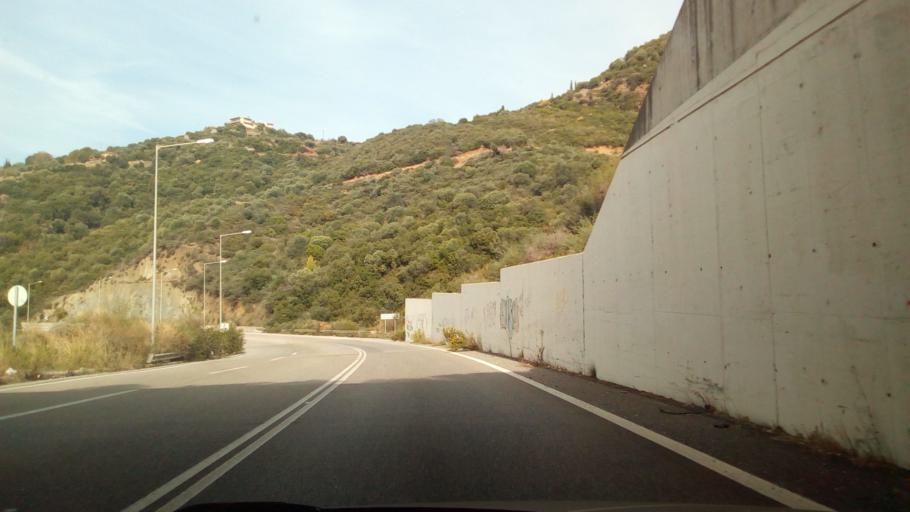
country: GR
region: West Greece
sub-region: Nomos Aitolias kai Akarnanias
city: Nafpaktos
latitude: 38.4030
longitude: 21.8099
